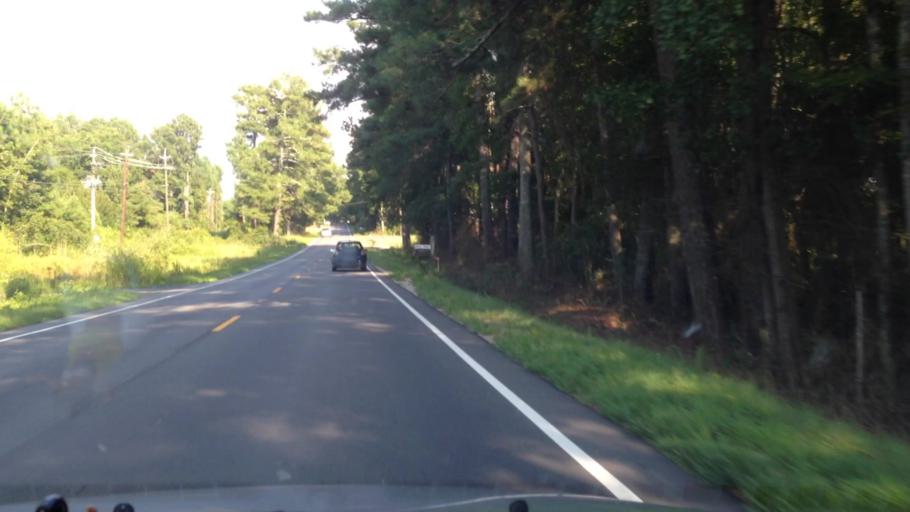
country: US
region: North Carolina
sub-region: Harnett County
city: Coats
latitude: 35.4133
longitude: -78.6936
